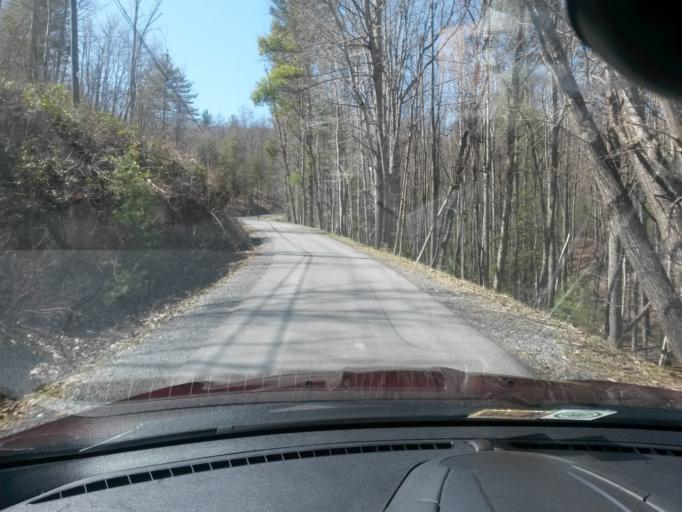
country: US
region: West Virginia
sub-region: Greenbrier County
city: White Sulphur Springs
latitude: 37.6721
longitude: -80.3185
